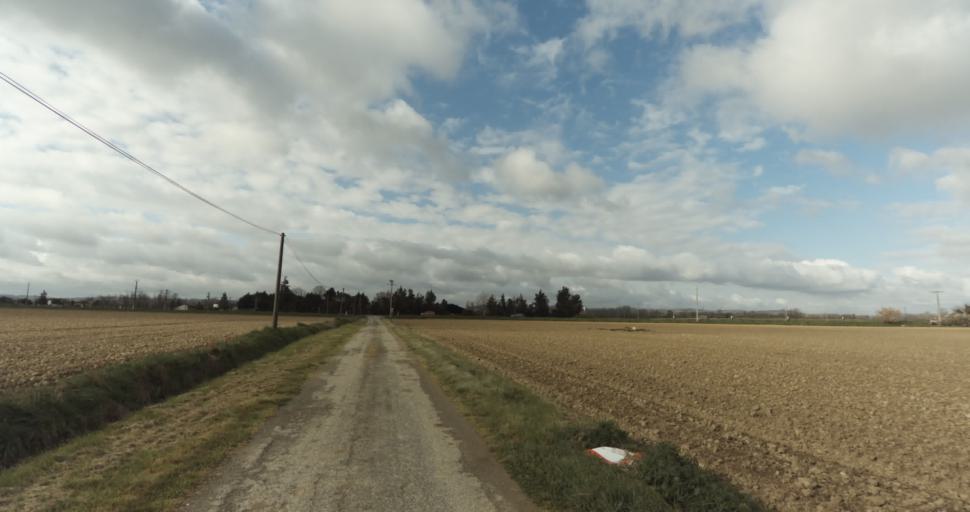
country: FR
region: Midi-Pyrenees
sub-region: Departement de la Haute-Garonne
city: Miremont
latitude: 43.3818
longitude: 1.4457
